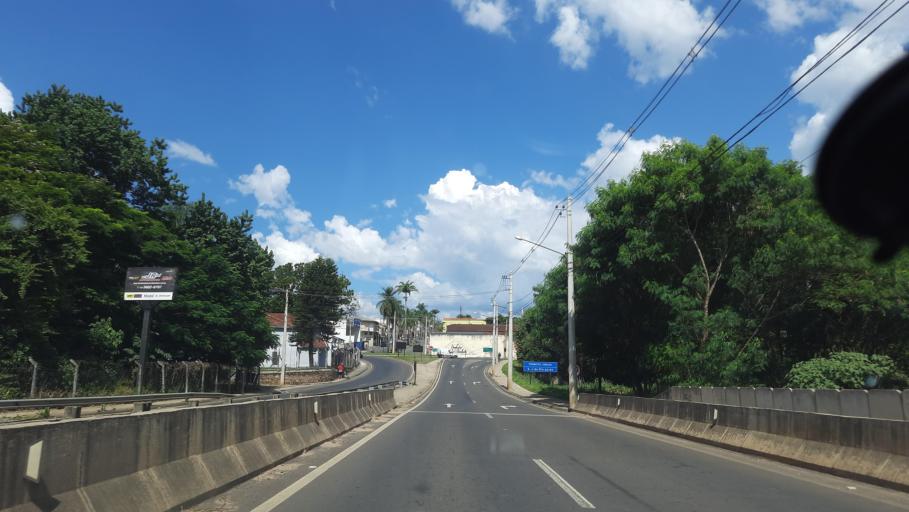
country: BR
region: Sao Paulo
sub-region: Sao Jose Do Rio Pardo
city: Sao Jose do Rio Pardo
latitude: -21.6021
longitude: -46.9034
